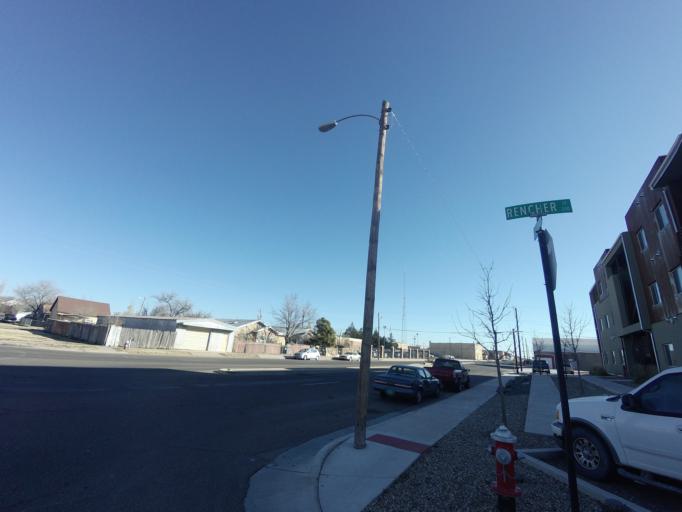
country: US
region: New Mexico
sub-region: Curry County
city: Clovis
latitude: 34.4006
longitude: -103.2092
